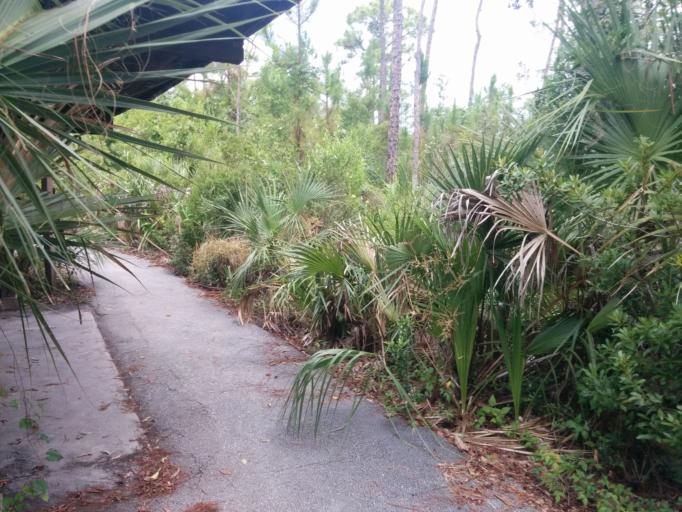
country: US
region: Florida
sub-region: Miami-Dade County
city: Florida City
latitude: 25.4234
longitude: -80.6795
